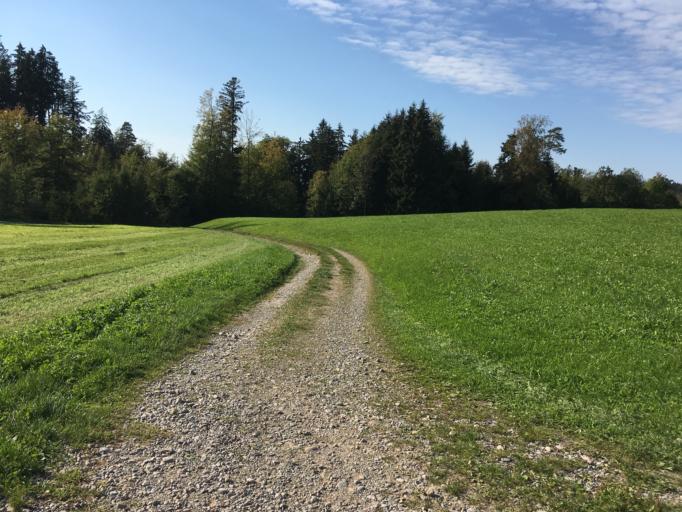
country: CH
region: Zurich
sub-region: Bezirk Hinwil
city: Wetzikon / Kempten
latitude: 47.3441
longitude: 8.8243
